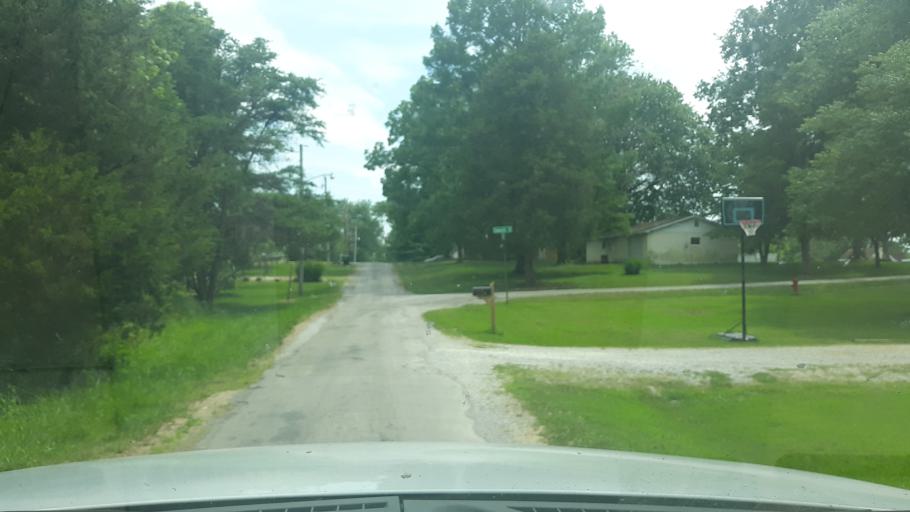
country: US
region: Illinois
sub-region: Saline County
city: Harrisburg
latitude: 37.8445
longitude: -88.6116
